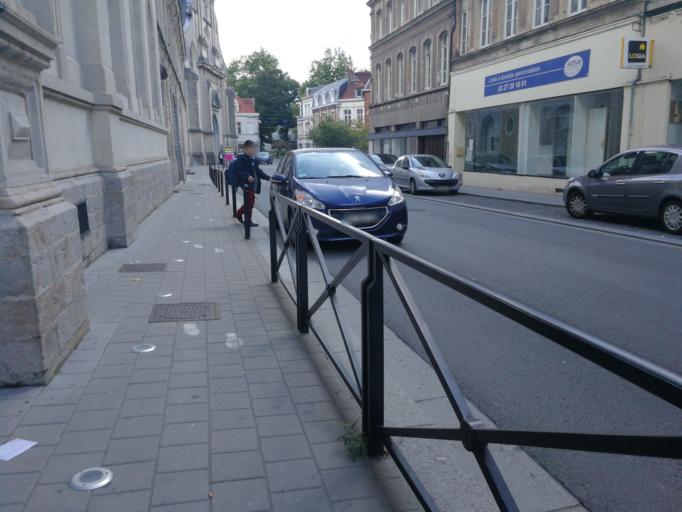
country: FR
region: Nord-Pas-de-Calais
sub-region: Departement du Nord
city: Valenciennes
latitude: 50.3599
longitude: 3.5189
